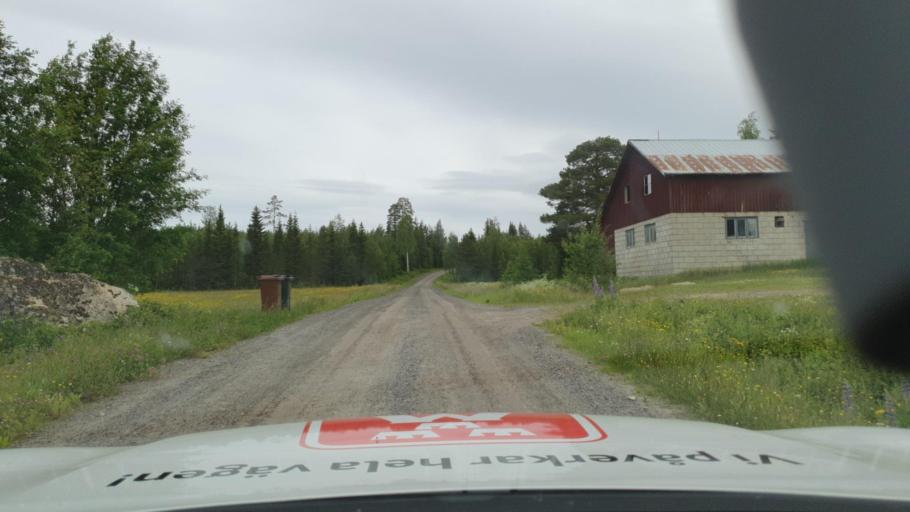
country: SE
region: Vaesterbotten
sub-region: Skelleftea Kommun
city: Burtraesk
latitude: 64.3527
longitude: 20.6126
